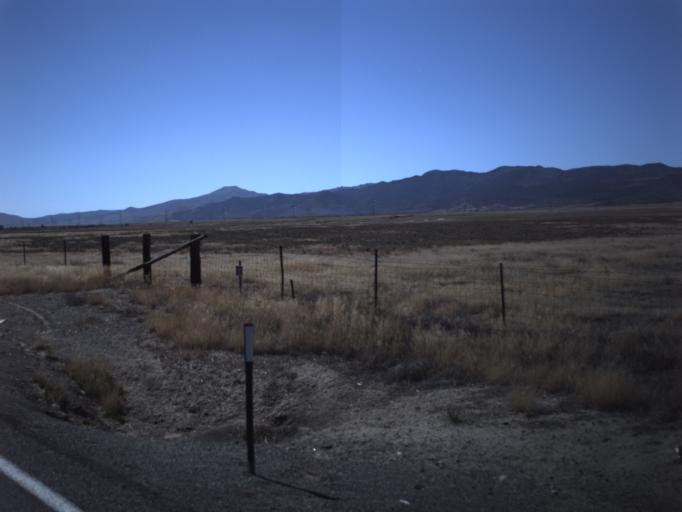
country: US
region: Utah
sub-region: Utah County
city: Genola
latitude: 39.9759
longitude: -111.9570
